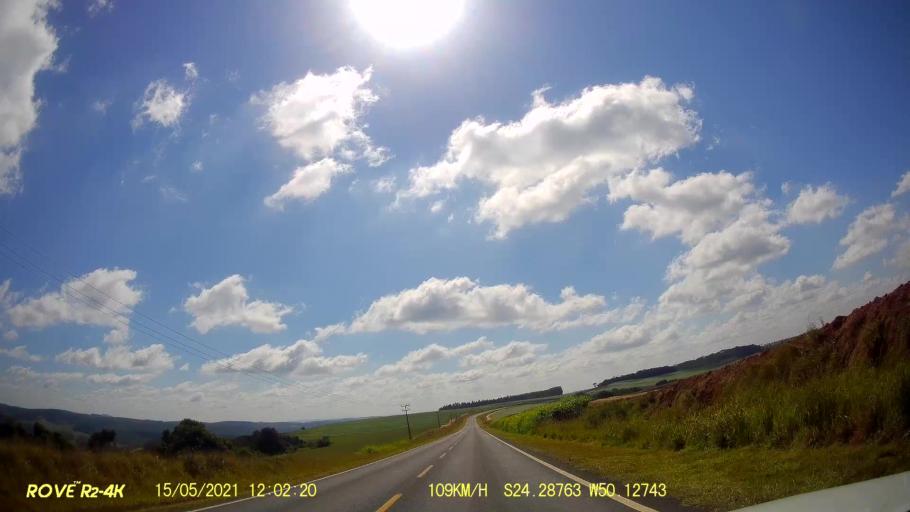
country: BR
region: Parana
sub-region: Pirai Do Sul
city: Pirai do Sul
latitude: -24.2878
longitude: -50.1277
